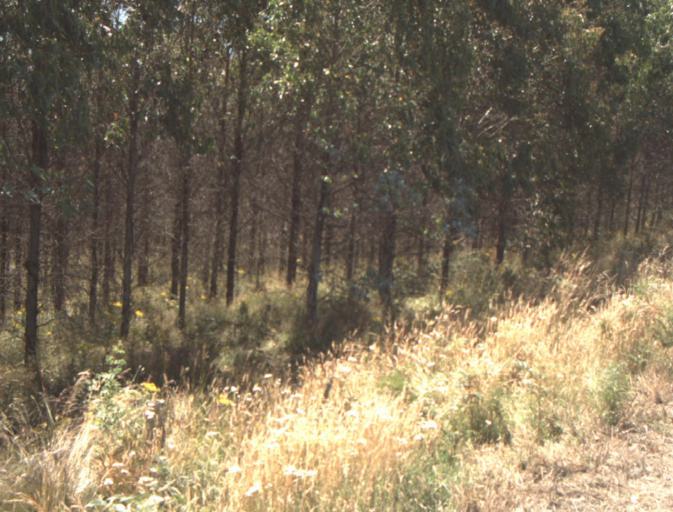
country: AU
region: Tasmania
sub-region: Dorset
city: Scottsdale
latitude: -41.3472
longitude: 147.4538
